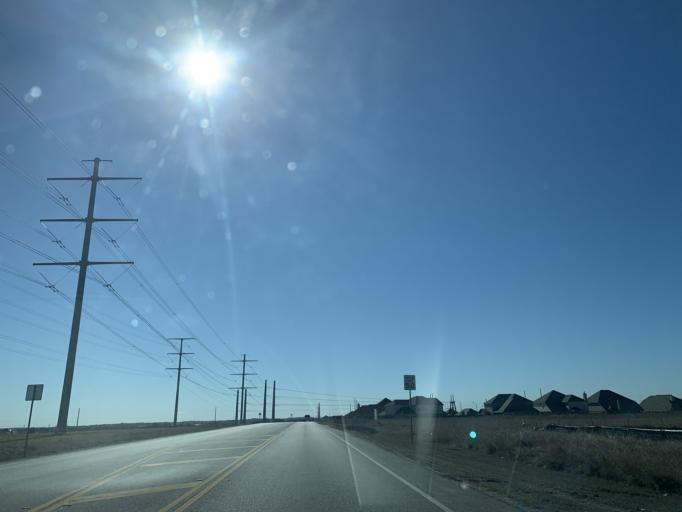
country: US
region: Texas
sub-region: Williamson County
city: Hutto
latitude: 30.5564
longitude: -97.5592
